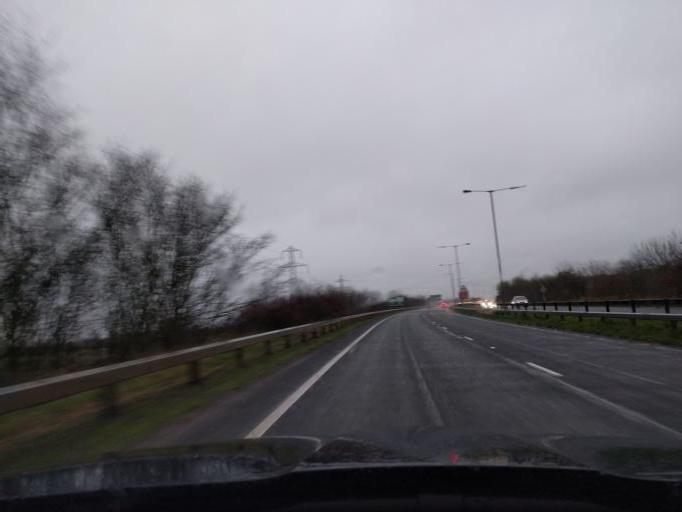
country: GB
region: England
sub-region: Northumberland
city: Newbiggin-by-the-Sea
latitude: 55.1757
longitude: -1.5303
